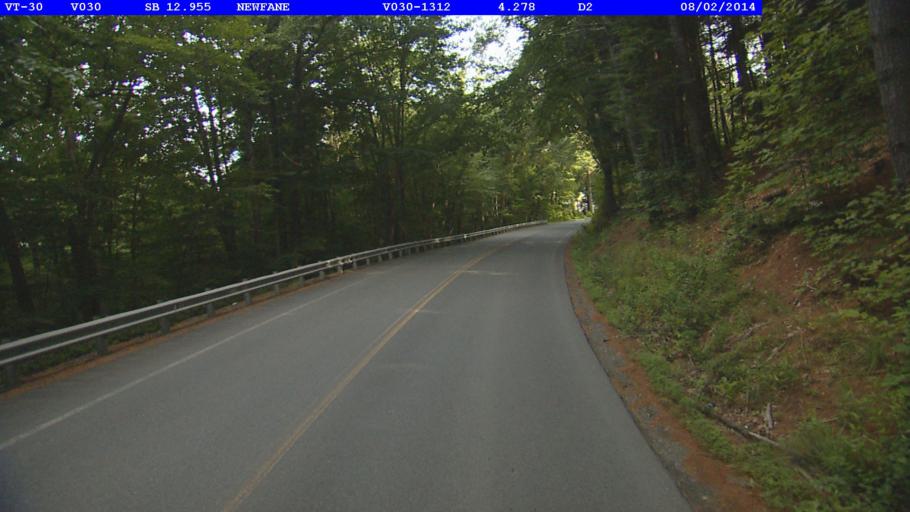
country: US
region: Vermont
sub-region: Windham County
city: Newfane
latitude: 43.0027
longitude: -72.6431
